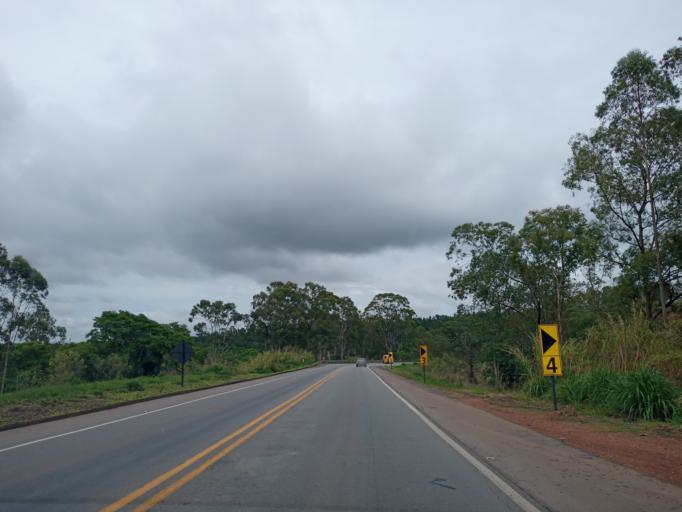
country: BR
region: Minas Gerais
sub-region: Campos Altos
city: Campos Altos
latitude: -19.6663
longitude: -46.1529
